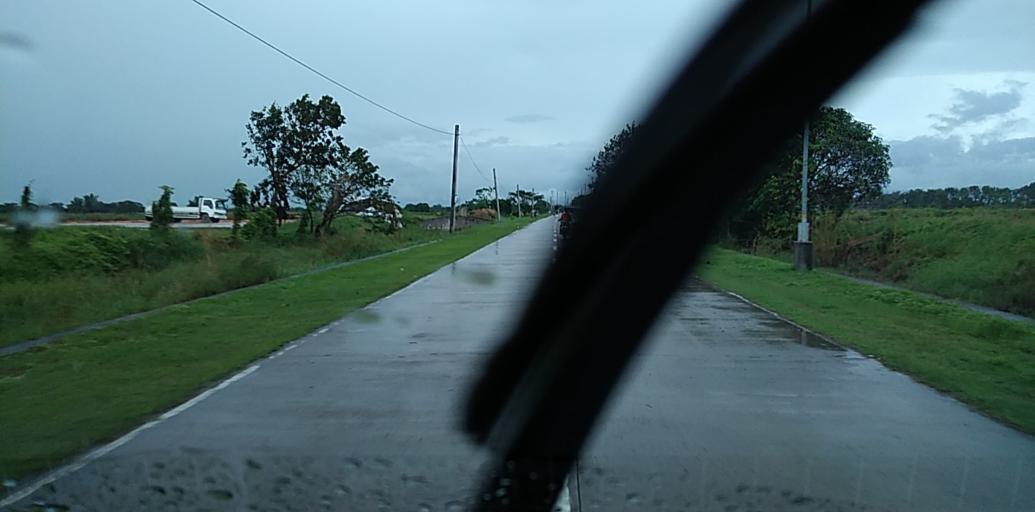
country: PH
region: Central Luzon
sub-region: Province of Pampanga
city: Salapungan
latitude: 15.1325
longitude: 120.8924
